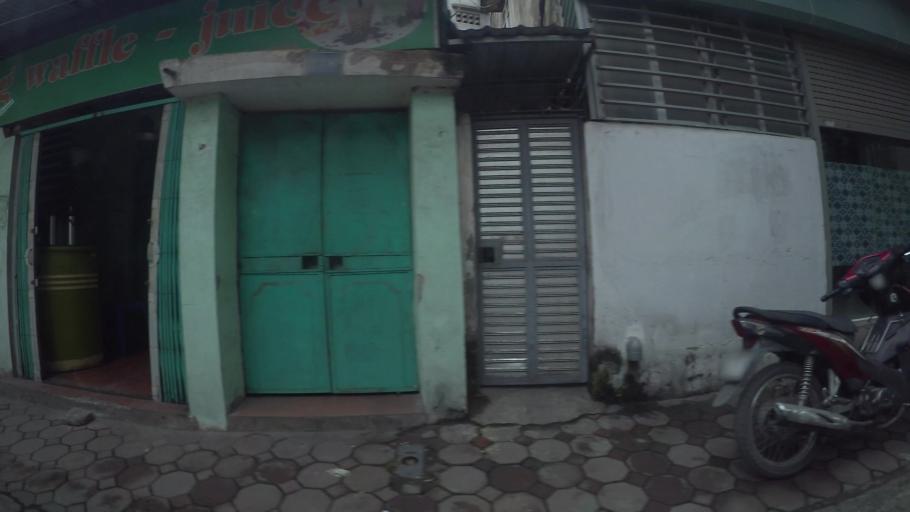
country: VN
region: Ha Noi
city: Hai BaTrung
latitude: 20.9994
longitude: 105.8563
